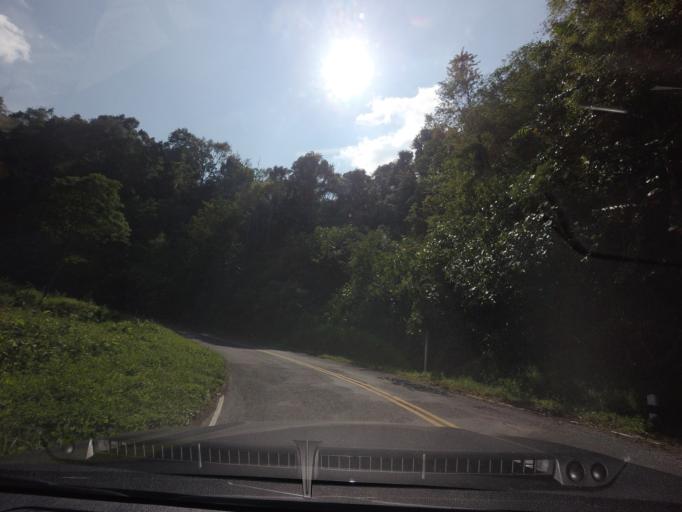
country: TH
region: Nan
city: Bo Kluea
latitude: 19.0578
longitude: 101.0878
